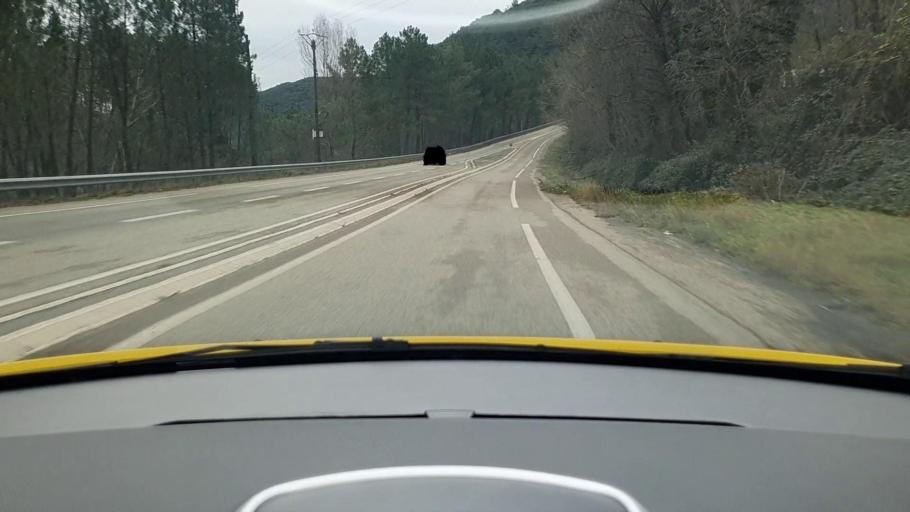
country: FR
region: Languedoc-Roussillon
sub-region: Departement du Gard
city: Laval-Pradel
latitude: 44.2239
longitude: 4.0810
